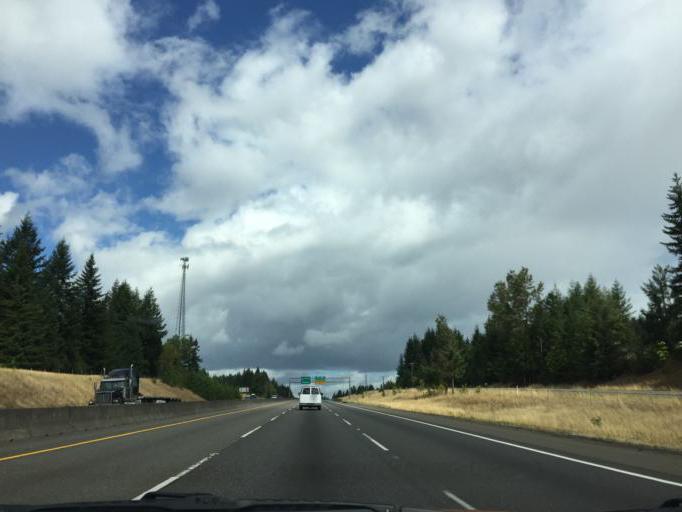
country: US
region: Washington
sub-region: Lewis County
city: Winlock
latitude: 46.4303
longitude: -122.8898
